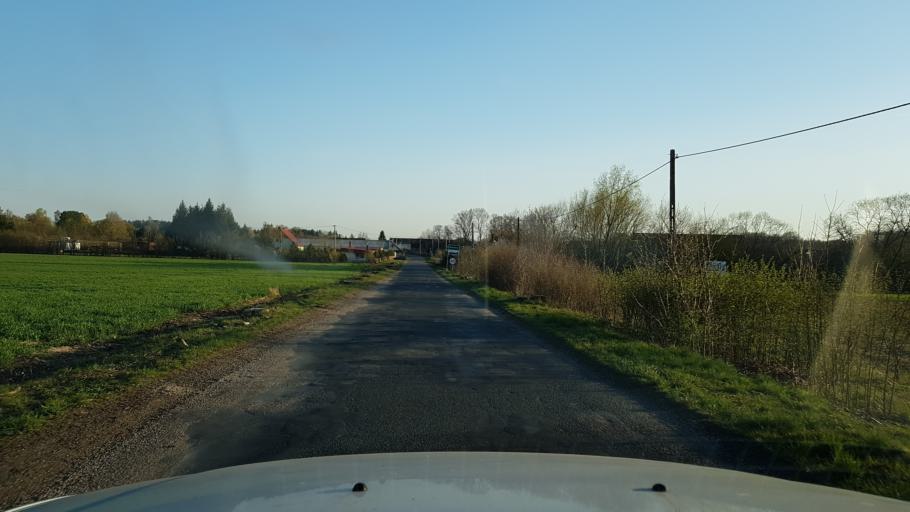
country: PL
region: West Pomeranian Voivodeship
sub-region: Powiat bialogardzki
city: Bialogard
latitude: 54.0289
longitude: 15.9887
